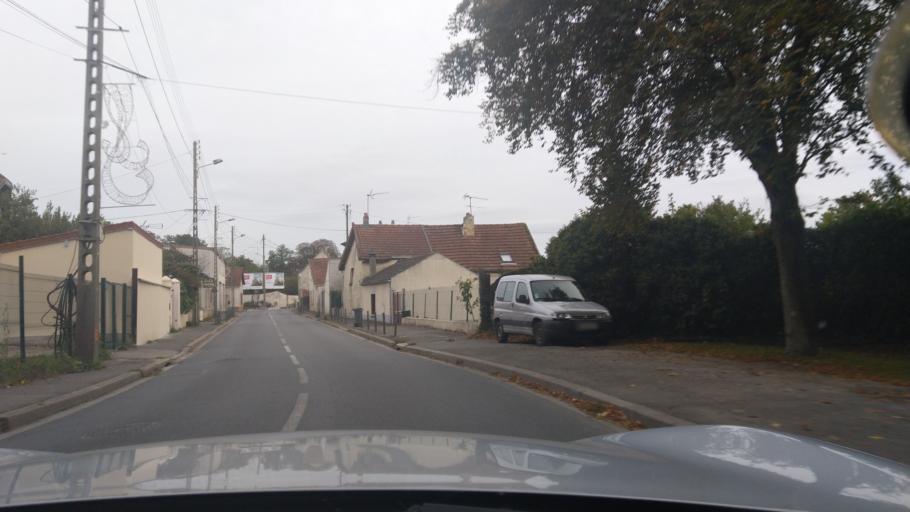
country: FR
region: Ile-de-France
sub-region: Departement de Seine-Saint-Denis
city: Villepinte
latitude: 48.9832
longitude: 2.5543
